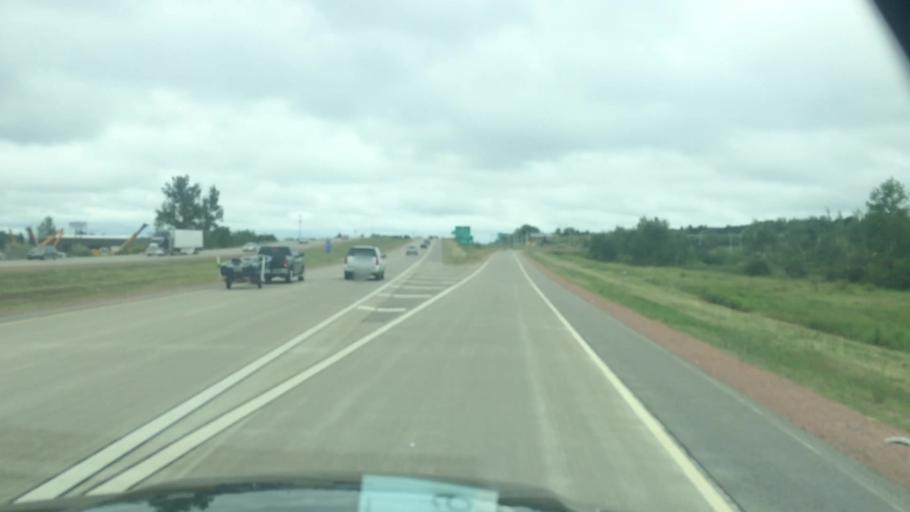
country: US
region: Wisconsin
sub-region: Marathon County
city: Wausau
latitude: 44.9960
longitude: -89.6578
